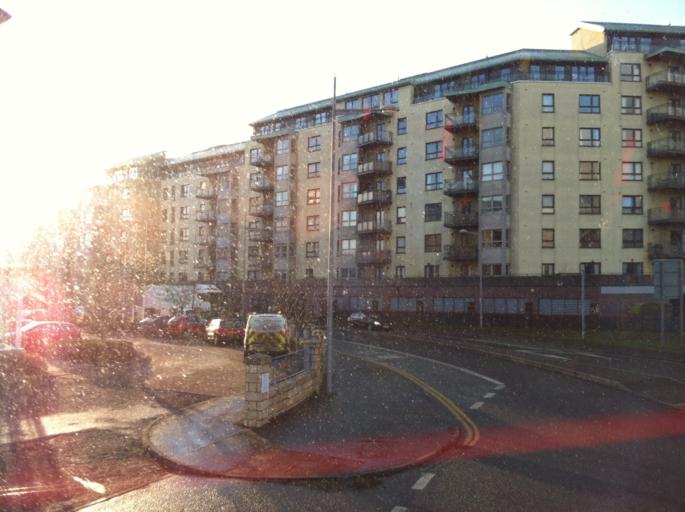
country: GB
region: Scotland
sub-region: West Lothian
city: Seafield
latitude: 55.9792
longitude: -3.1791
